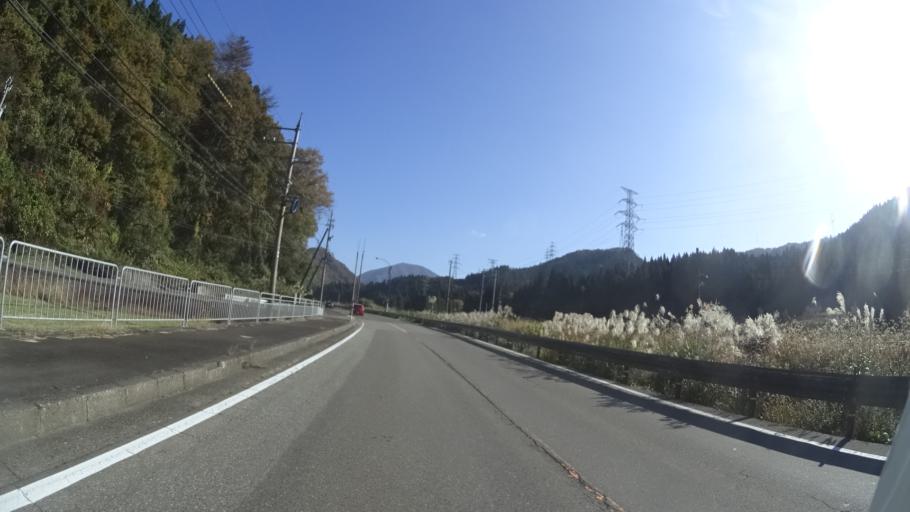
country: JP
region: Fukui
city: Ono
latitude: 36.0020
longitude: 136.4052
